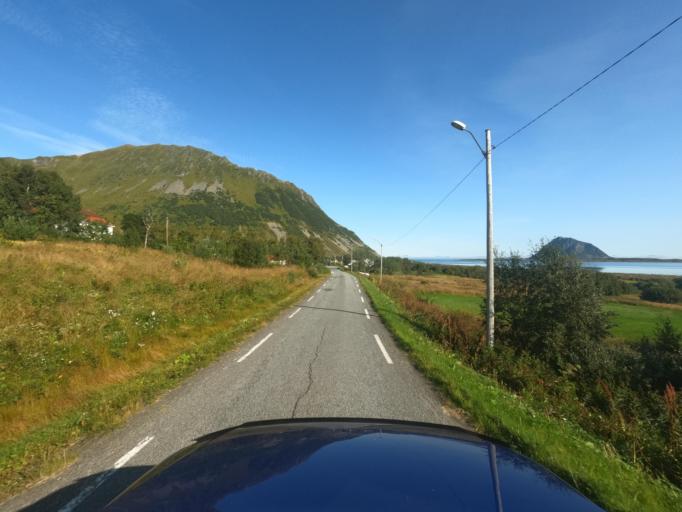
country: NO
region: Nordland
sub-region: Vestvagoy
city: Evjen
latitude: 68.2921
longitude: 14.0009
